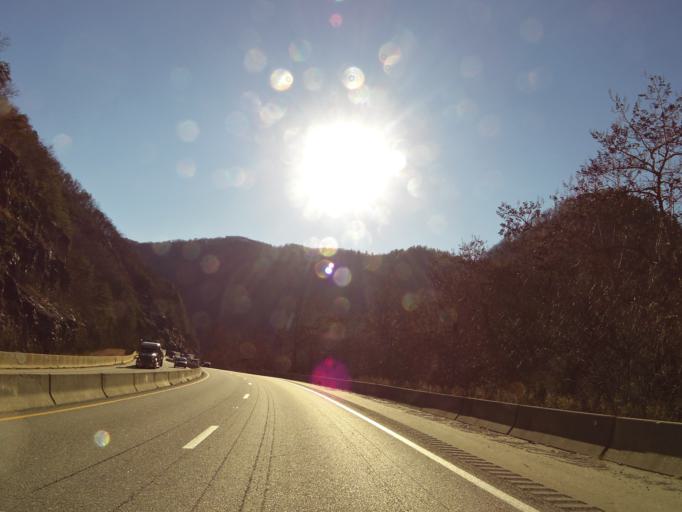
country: US
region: North Carolina
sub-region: Haywood County
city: Cove Creek
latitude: 35.7558
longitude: -83.0703
